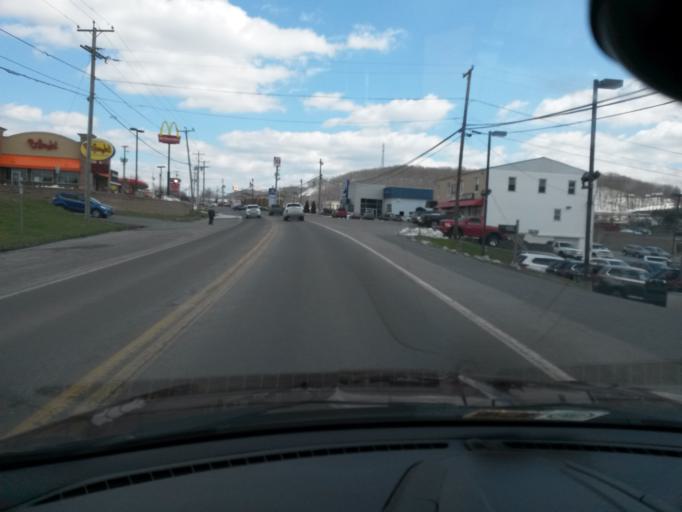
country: US
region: West Virginia
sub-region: Mercer County
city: Princeton
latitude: 37.3628
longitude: -81.0602
